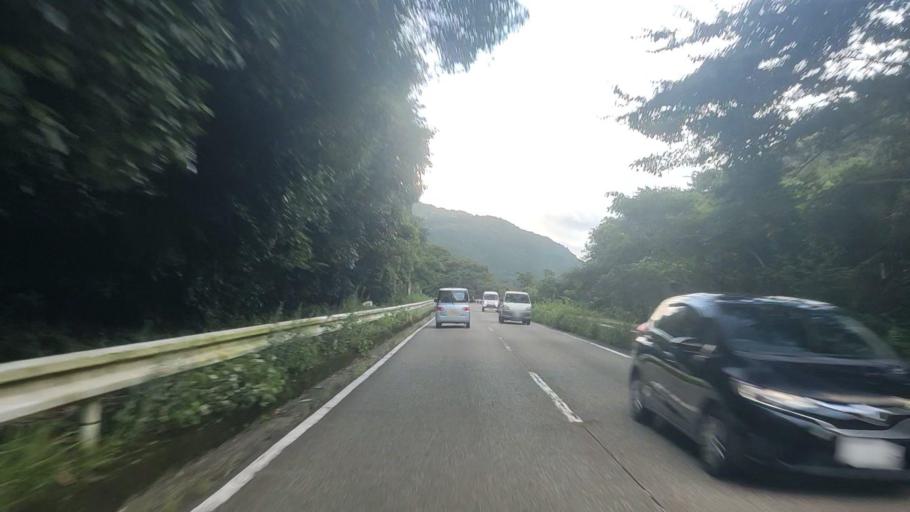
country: JP
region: Wakayama
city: Tanabe
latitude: 33.7647
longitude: 135.5002
